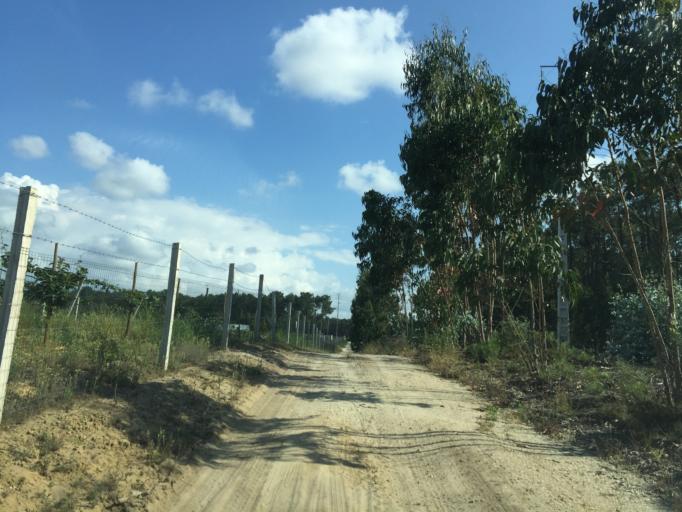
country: PT
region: Leiria
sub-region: Leiria
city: Monte Redondo
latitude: 39.9451
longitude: -8.8258
